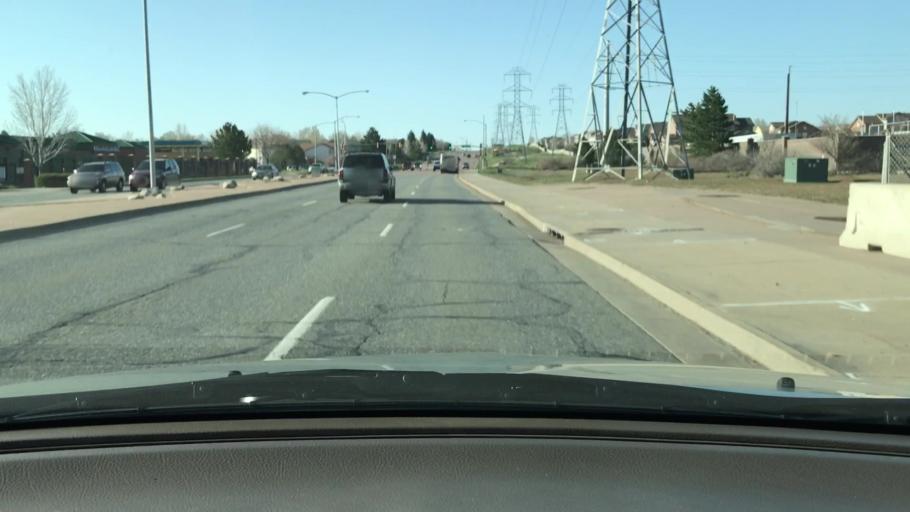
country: US
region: Colorado
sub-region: Adams County
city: Aurora
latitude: 39.6672
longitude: -104.7723
